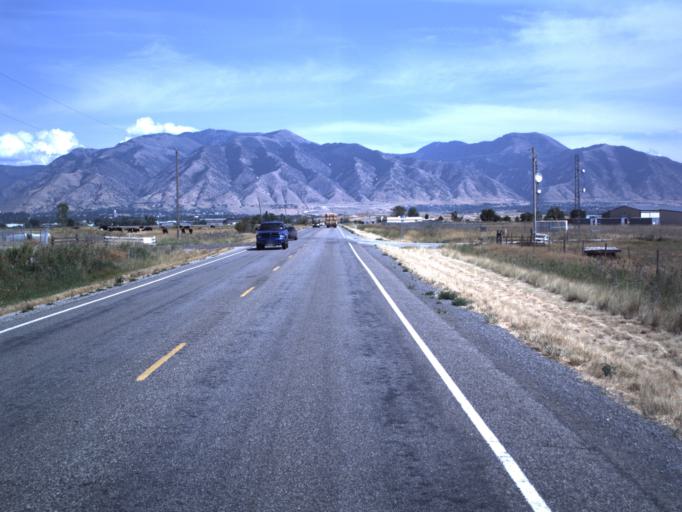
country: US
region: Utah
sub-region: Cache County
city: Benson
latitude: 41.7382
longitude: -111.8974
